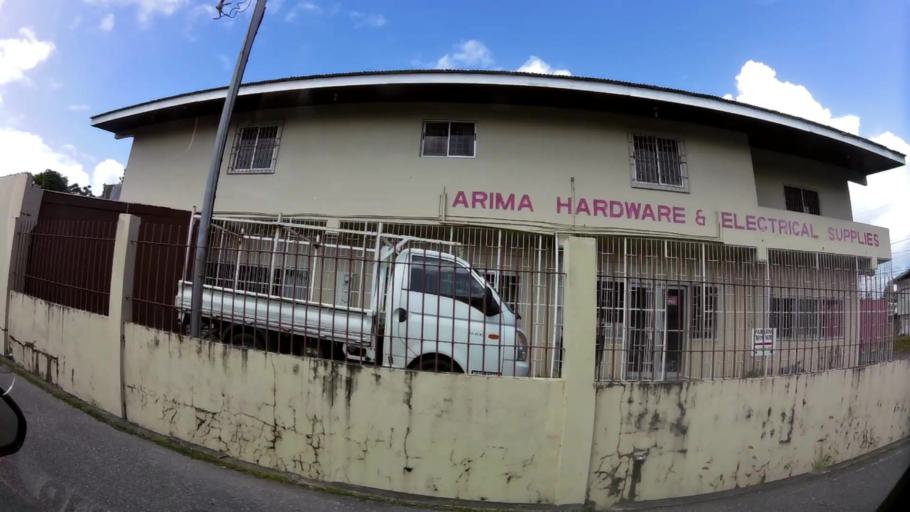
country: TT
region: Borough of Arima
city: Arima
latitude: 10.6311
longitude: -61.2761
